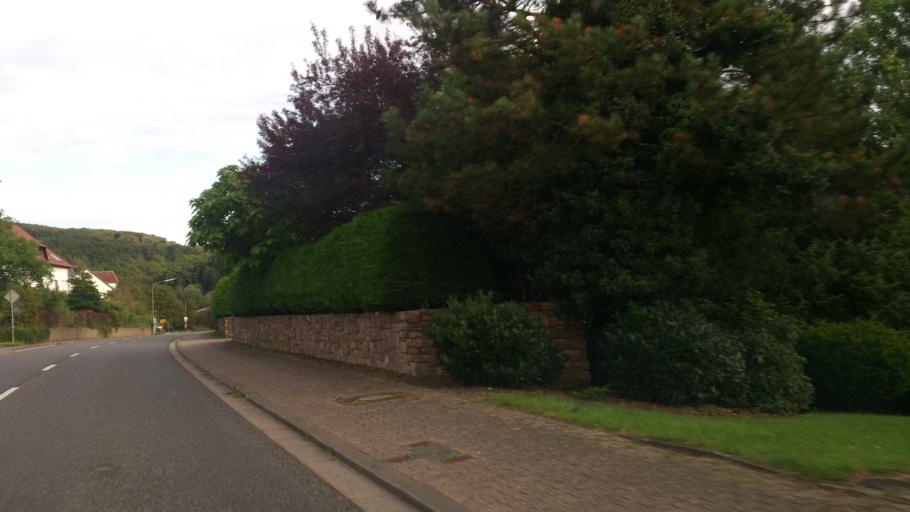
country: DE
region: Saarland
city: Tholey
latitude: 49.5382
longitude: 6.9858
